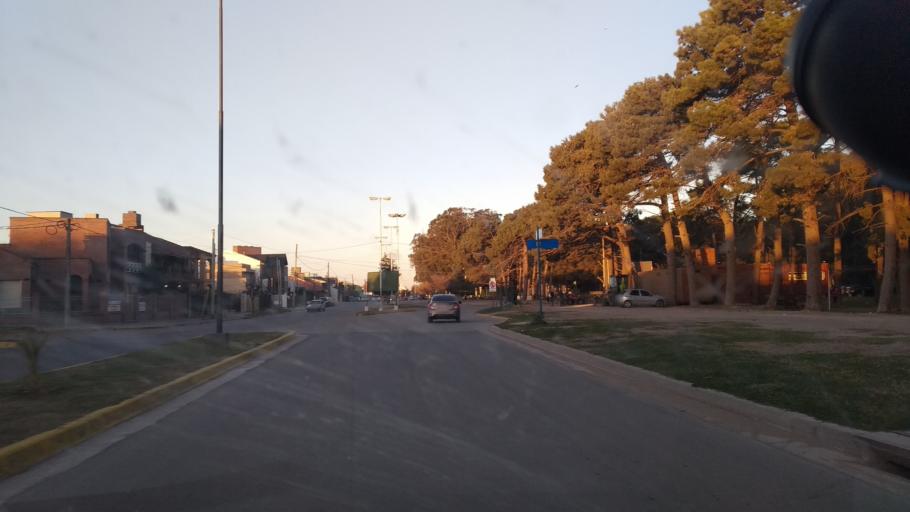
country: AR
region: Buenos Aires
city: Necochea
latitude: -38.5825
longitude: -58.7425
